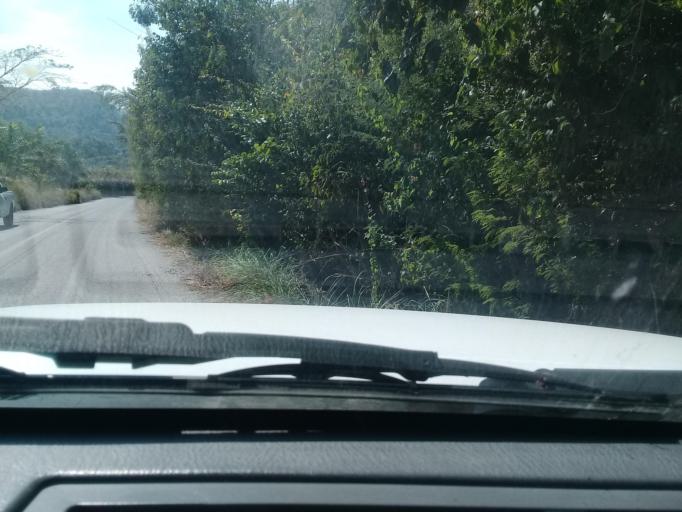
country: MX
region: Veracruz
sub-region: Emiliano Zapata
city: Plan del Rio
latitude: 19.4266
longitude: -96.6077
